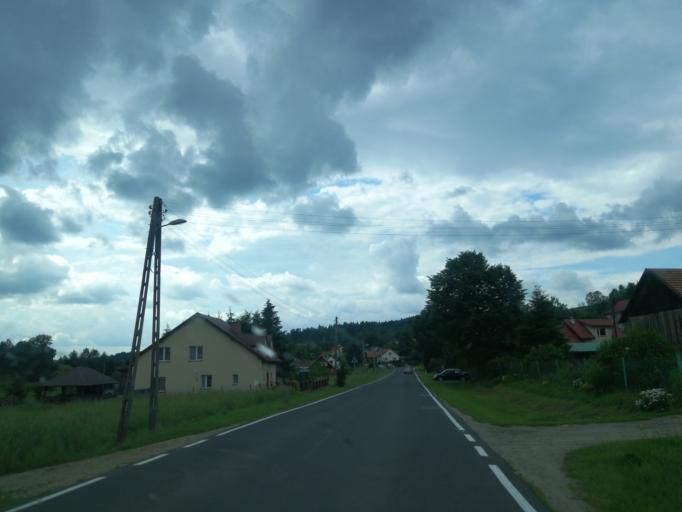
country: PL
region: Subcarpathian Voivodeship
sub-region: Powiat leski
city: Olszanica
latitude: 49.4462
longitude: 22.4445
